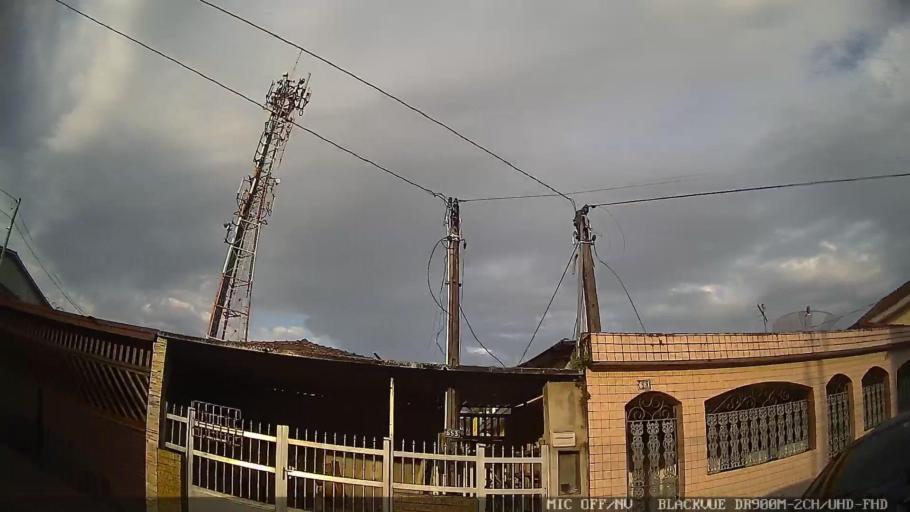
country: BR
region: Sao Paulo
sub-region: Cubatao
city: Cubatao
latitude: -23.8978
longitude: -46.4270
